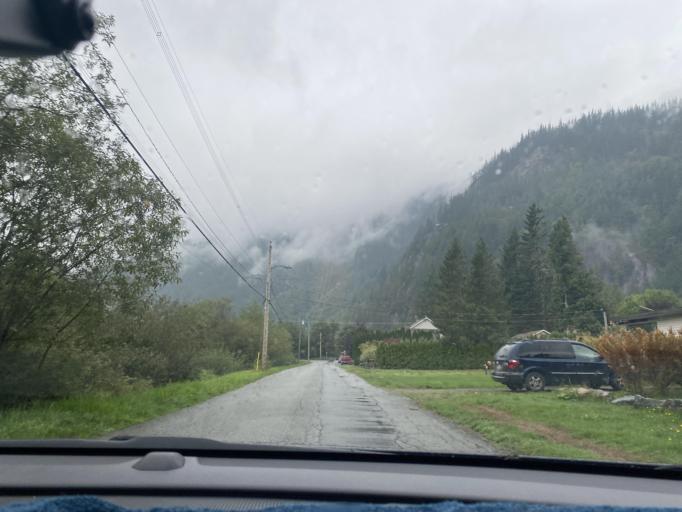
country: CA
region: British Columbia
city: Agassiz
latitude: 49.2805
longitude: -121.7807
